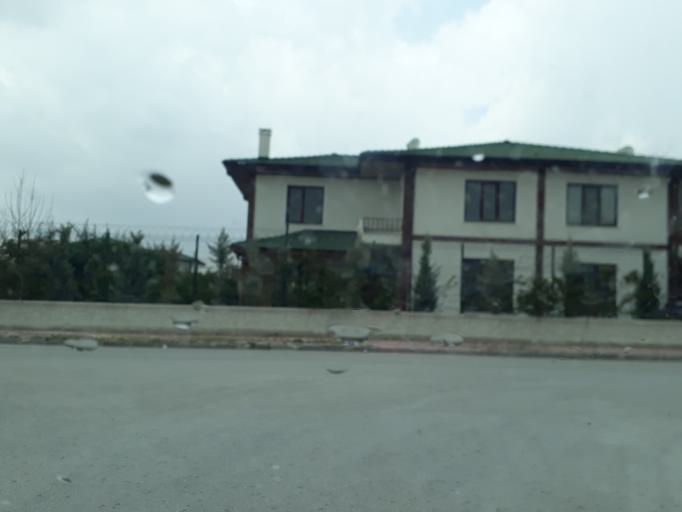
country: TR
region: Konya
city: Sille
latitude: 37.9197
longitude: 32.4621
